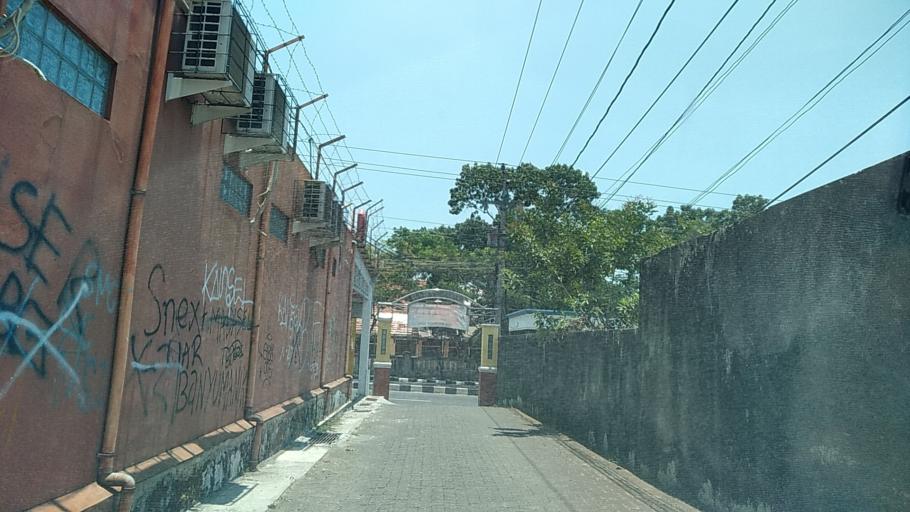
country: ID
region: Central Java
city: Ungaran
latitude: -7.0715
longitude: 110.4116
